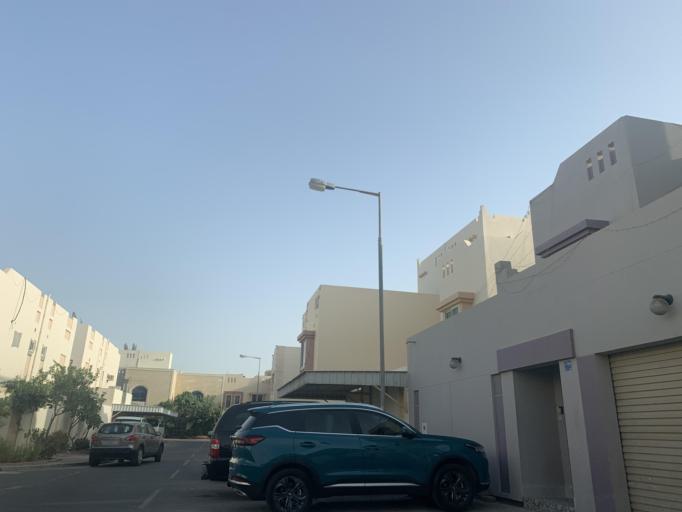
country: BH
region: Manama
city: Jidd Hafs
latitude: 26.2224
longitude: 50.5483
